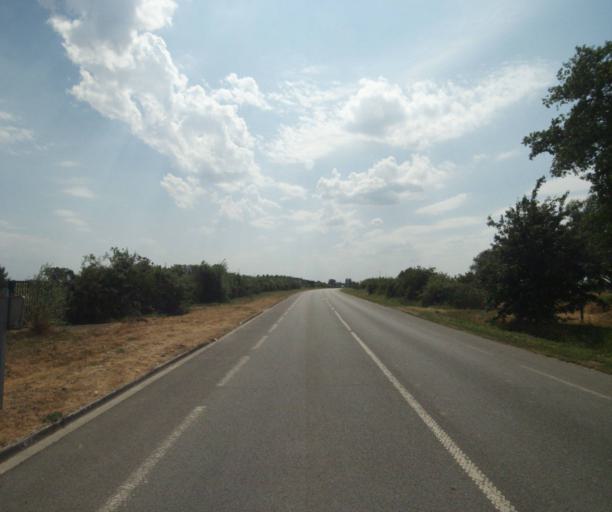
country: FR
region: Nord-Pas-de-Calais
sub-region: Departement du Nord
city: Wervicq-Sud
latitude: 50.7667
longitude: 3.0303
